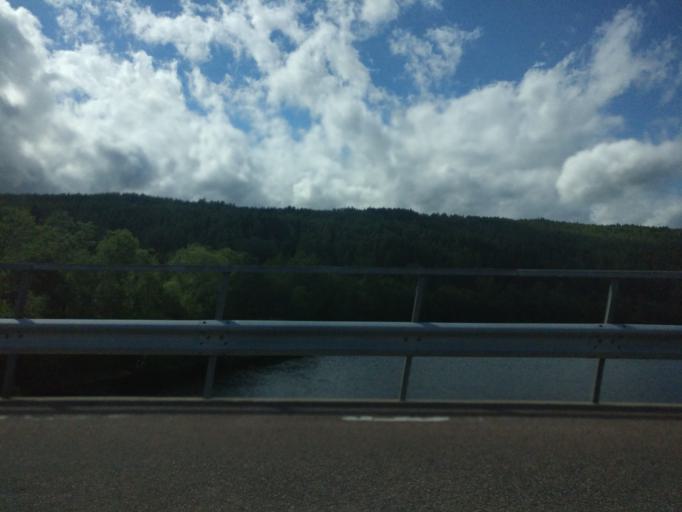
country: SE
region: Vaermland
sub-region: Hagfors Kommun
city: Ekshaerad
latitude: 60.2892
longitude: 13.3946
